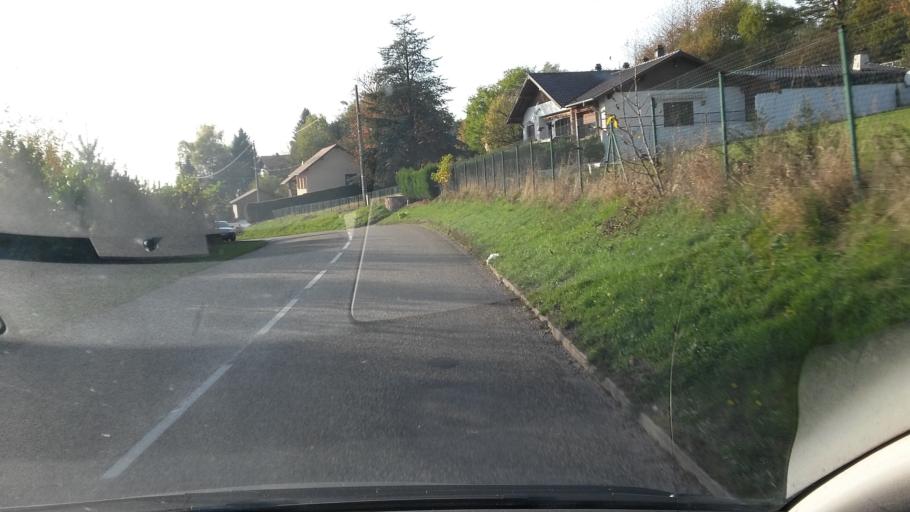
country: FR
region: Lorraine
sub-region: Departement de la Moselle
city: Dabo
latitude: 48.6874
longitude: 7.2114
